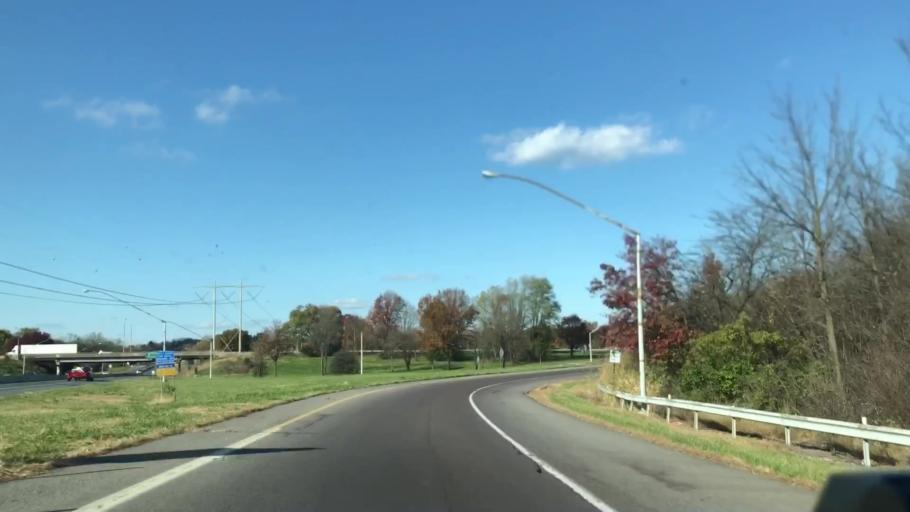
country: US
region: Pennsylvania
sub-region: Lehigh County
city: Wescosville
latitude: 40.5978
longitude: -75.5578
